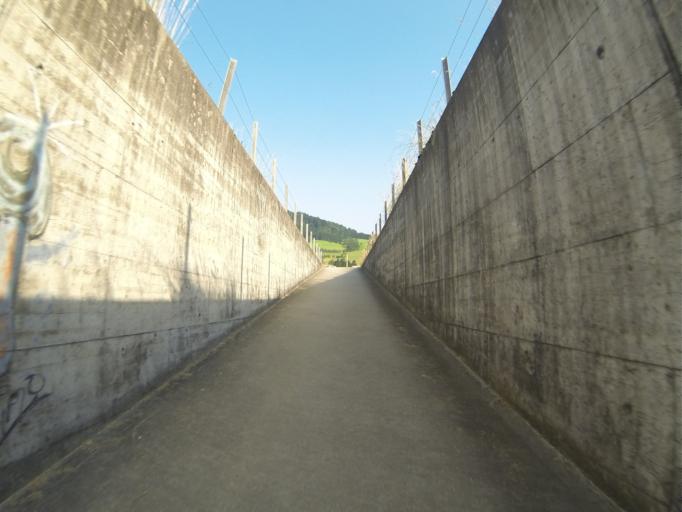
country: CH
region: Lucerne
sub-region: Lucerne-Land District
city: Buchrain
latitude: 47.1012
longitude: 8.3684
